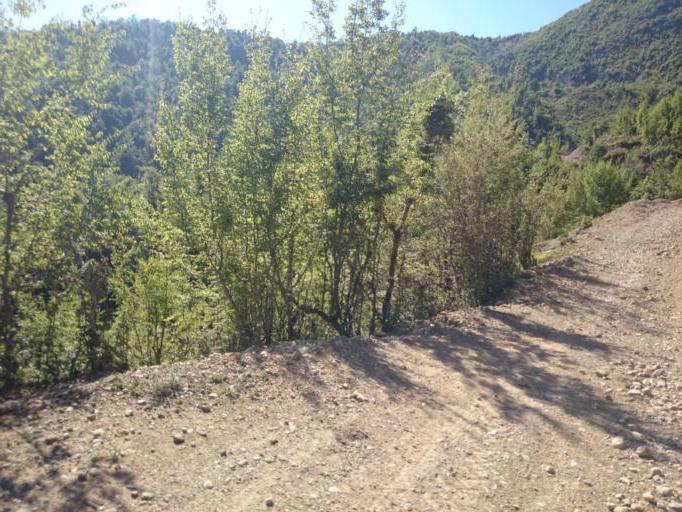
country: AL
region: Elbasan
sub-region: Rrethi i Gramshit
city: Porocan
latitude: 40.9302
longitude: 20.2781
